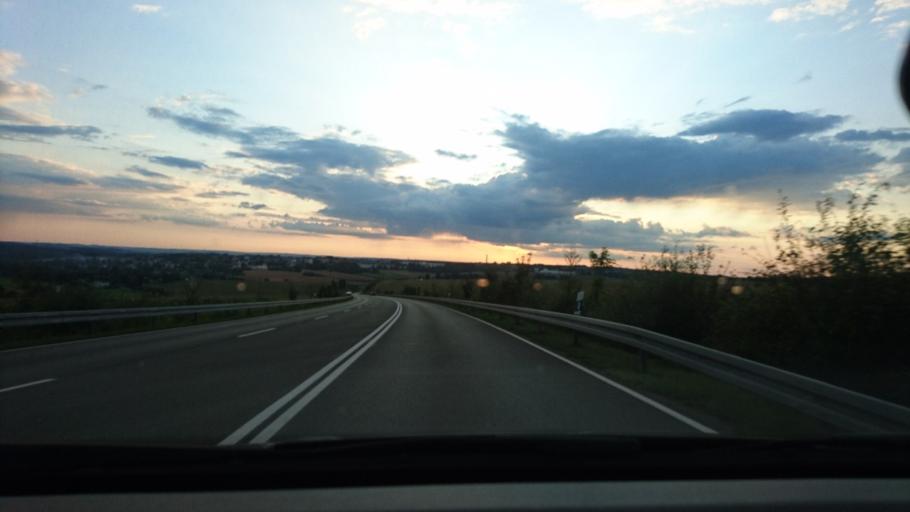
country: DE
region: Saxony
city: Treuen
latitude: 50.5470
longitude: 12.3317
